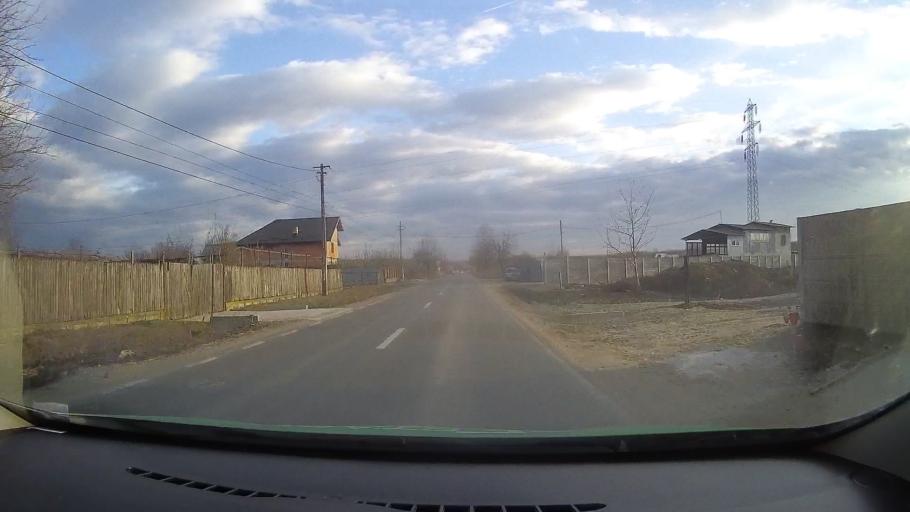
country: RO
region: Dambovita
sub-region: Comuna I. L. Caragiale
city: Ghirdoveni
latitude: 44.9574
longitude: 25.6575
